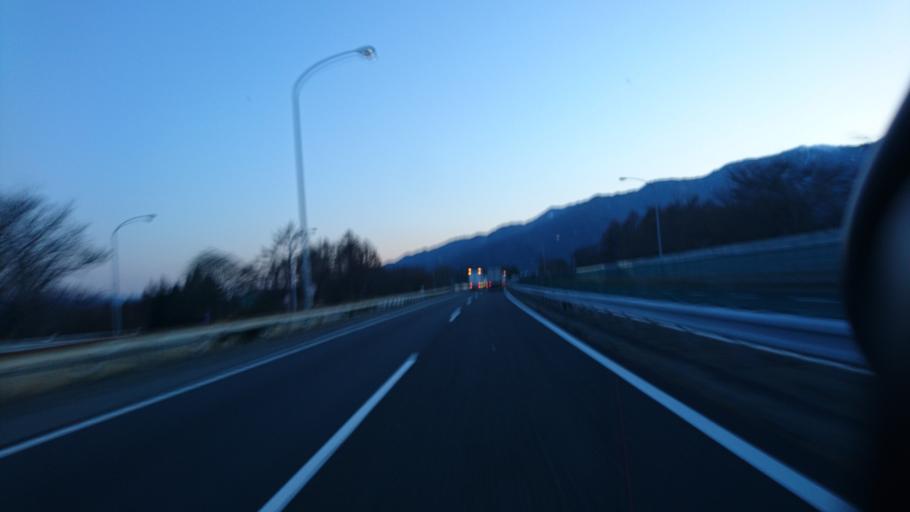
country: JP
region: Nagano
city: Ina
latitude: 35.8667
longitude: 137.9440
